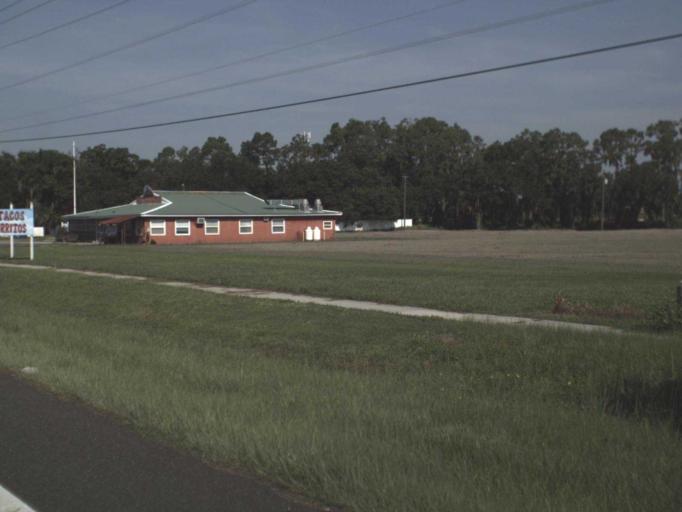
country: US
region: Florida
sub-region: Hillsborough County
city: Plant City
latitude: 27.9378
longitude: -82.1175
